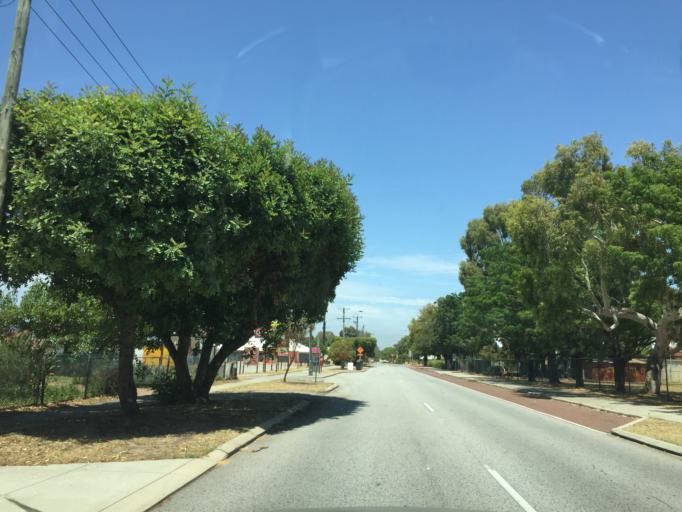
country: AU
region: Western Australia
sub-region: Canning
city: Queens Park
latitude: -31.9988
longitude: 115.9452
